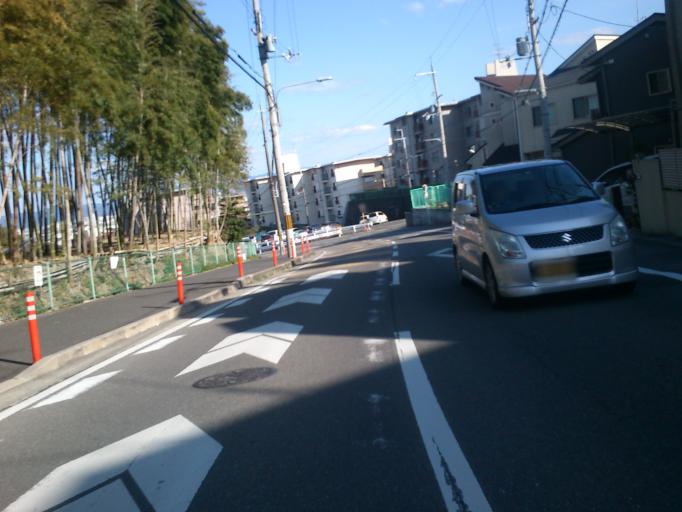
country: JP
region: Kyoto
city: Yawata
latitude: 34.9126
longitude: 135.6819
